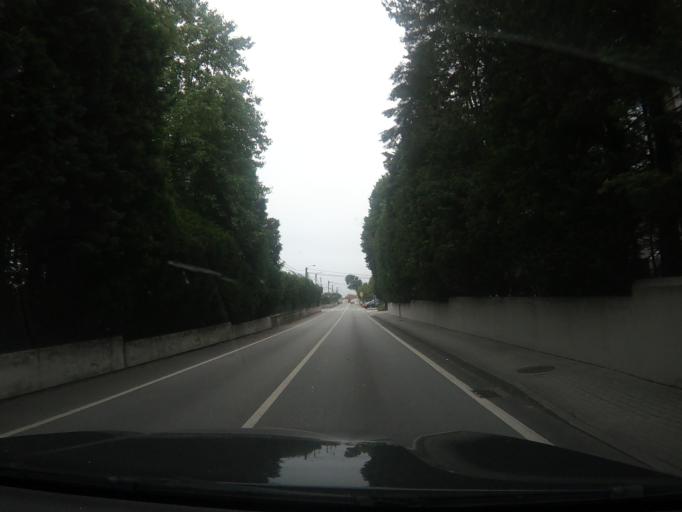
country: PT
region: Aveiro
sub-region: Santa Maria da Feira
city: Lamas
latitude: 40.9897
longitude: -8.5817
